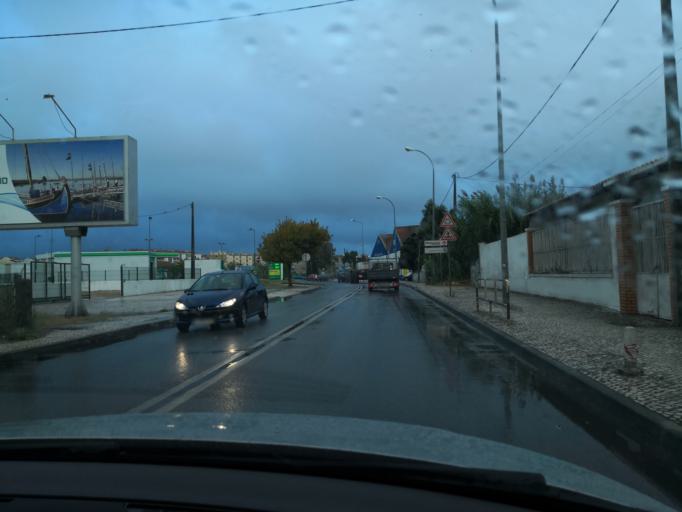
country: PT
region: Setubal
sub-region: Moita
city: Moita
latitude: 38.6479
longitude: -8.9947
